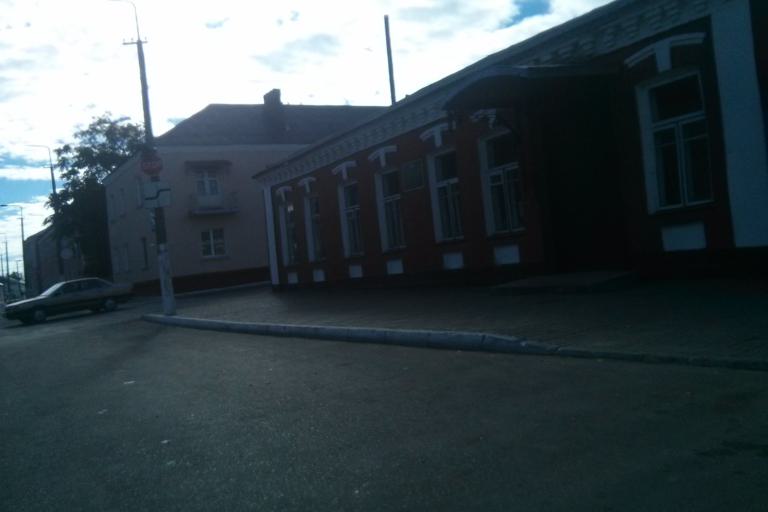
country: BY
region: Minsk
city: Chervyen'
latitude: 53.7142
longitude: 28.4160
